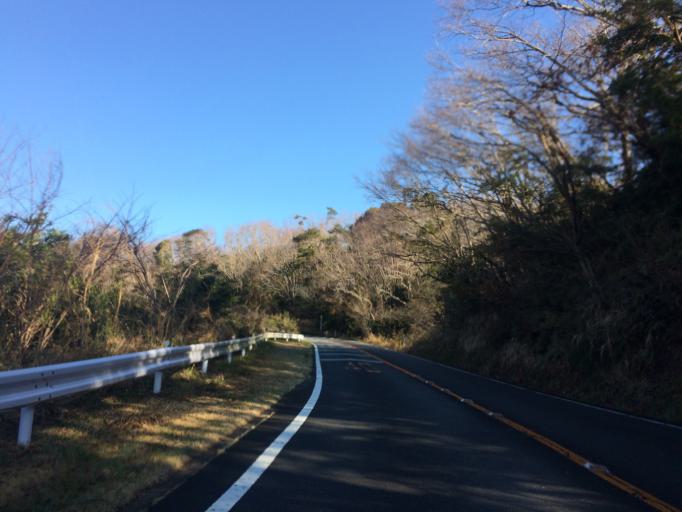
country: JP
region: Shizuoka
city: Shizuoka-shi
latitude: 34.9677
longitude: 138.4583
